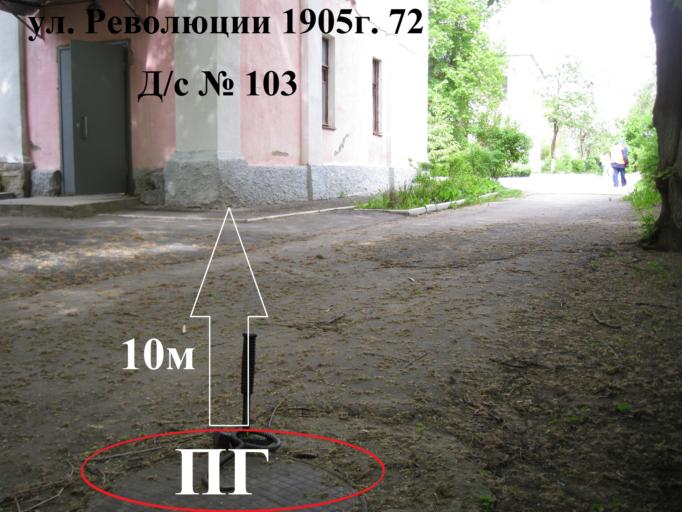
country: RU
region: Voronezj
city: Voronezh
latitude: 51.6699
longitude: 39.1859
